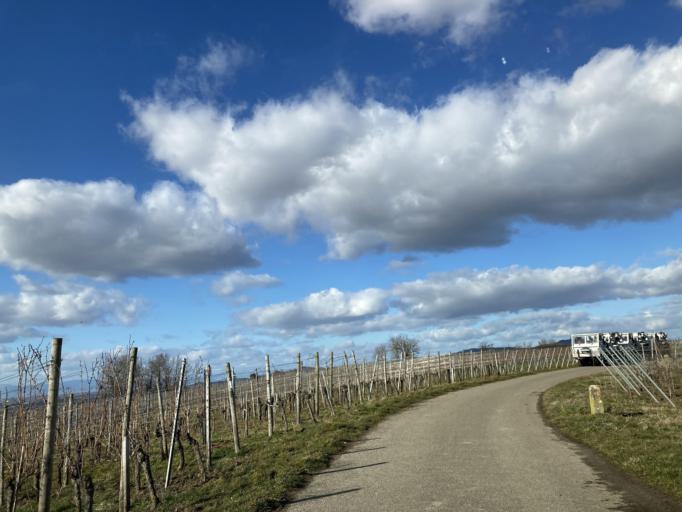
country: DE
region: Baden-Wuerttemberg
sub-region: Freiburg Region
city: Merdingen
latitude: 47.9986
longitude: 7.6751
